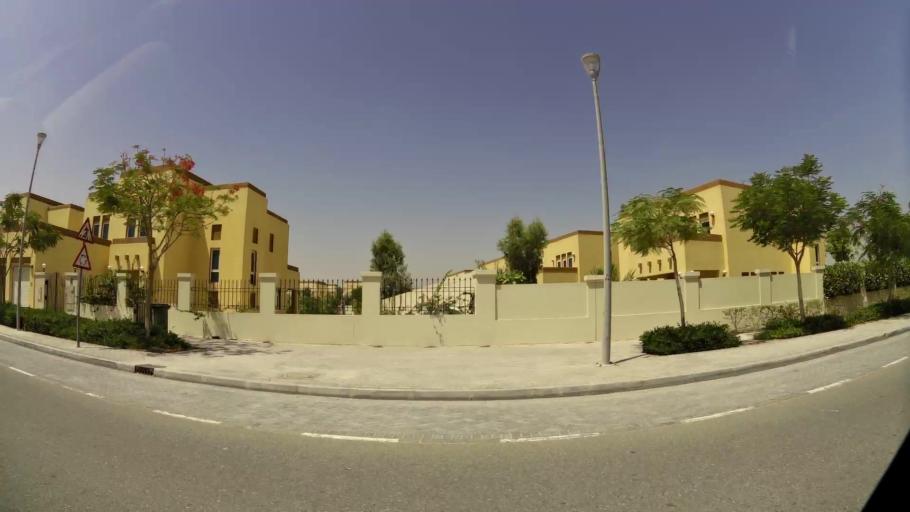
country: AE
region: Dubai
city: Dubai
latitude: 25.0404
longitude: 55.1596
